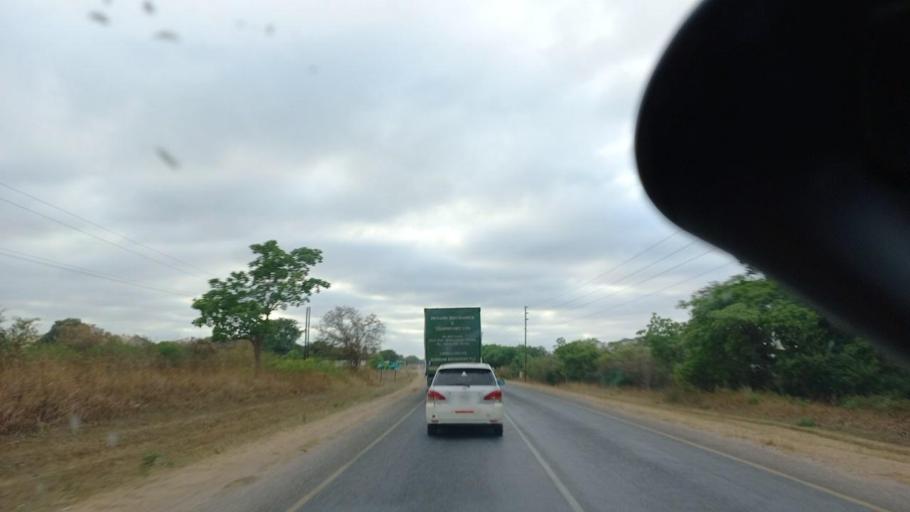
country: ZM
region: Lusaka
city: Chongwe
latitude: -15.3475
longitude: 28.5298
